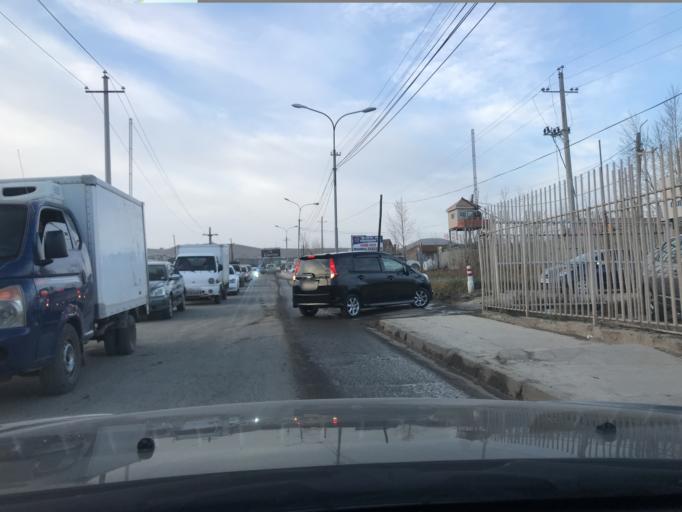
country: MN
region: Ulaanbaatar
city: Ulaanbaatar
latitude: 47.9284
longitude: 106.9979
